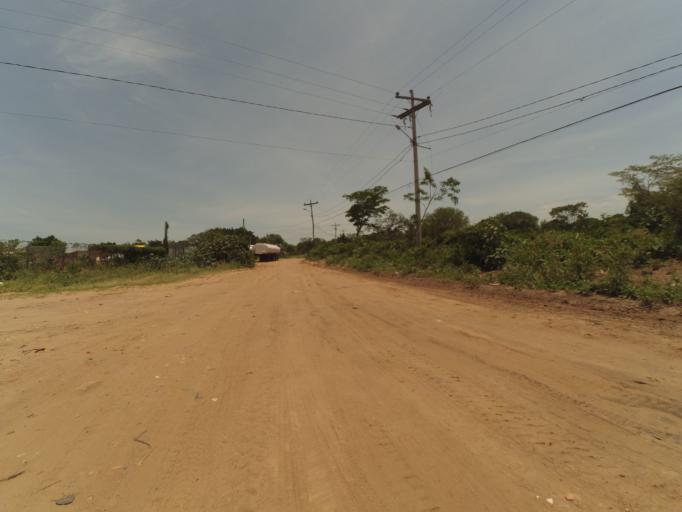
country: BO
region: Santa Cruz
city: Santa Cruz de la Sierra
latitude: -17.8304
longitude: -63.2522
